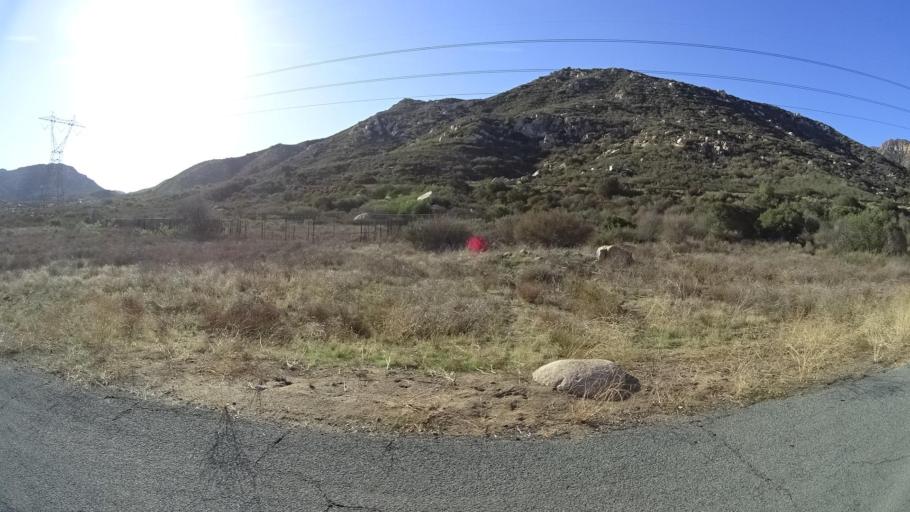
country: MX
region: Baja California
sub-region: Tecate
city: Lomas de Santa Anita
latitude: 32.6058
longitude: -116.6961
